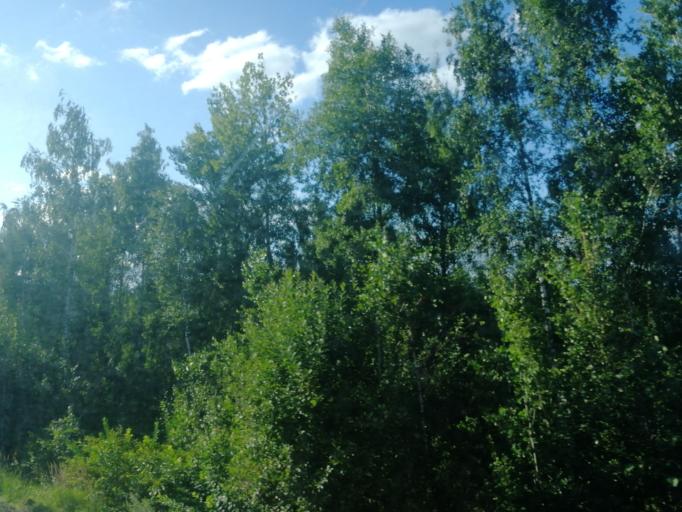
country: RU
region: Tula
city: Novogurovskiy
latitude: 54.2802
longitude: 37.2055
